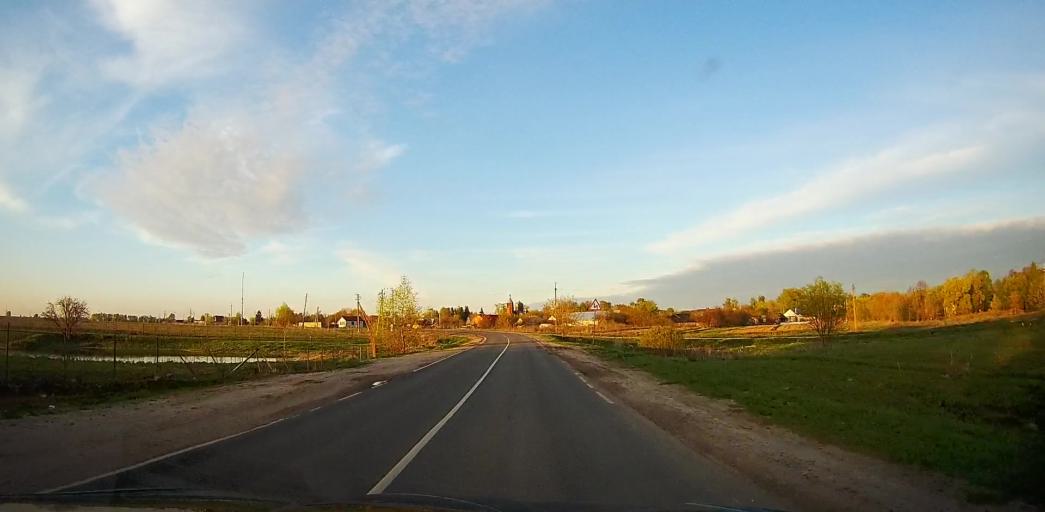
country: RU
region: Moskovskaya
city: Peski
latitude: 55.2125
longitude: 38.6648
